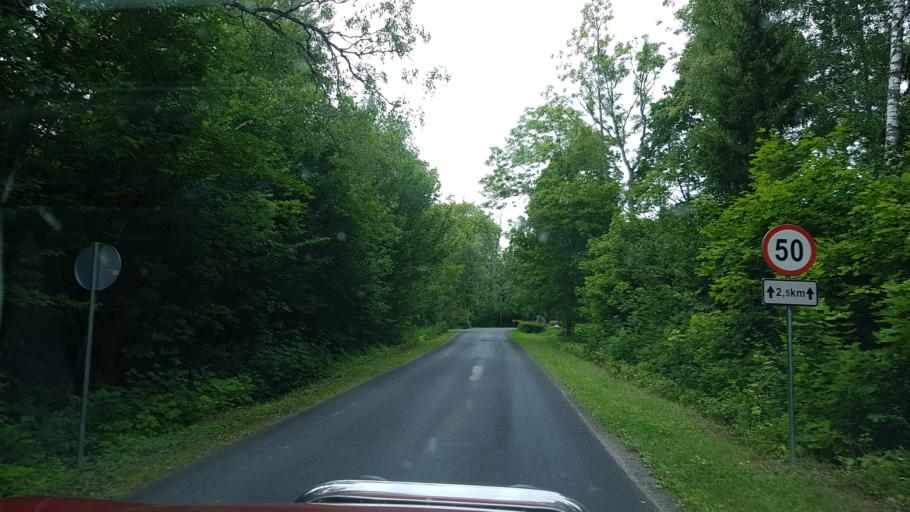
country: EE
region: Laeaene
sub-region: Ridala Parish
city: Uuemoisa
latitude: 59.0004
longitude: 23.7228
